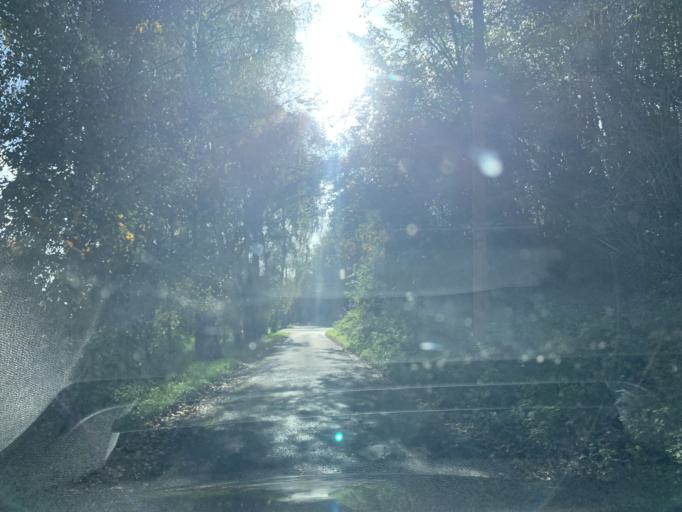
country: FR
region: Nord-Pas-de-Calais
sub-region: Departement du Nord
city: Neuville-Saint-Remy
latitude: 50.1856
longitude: 3.2317
